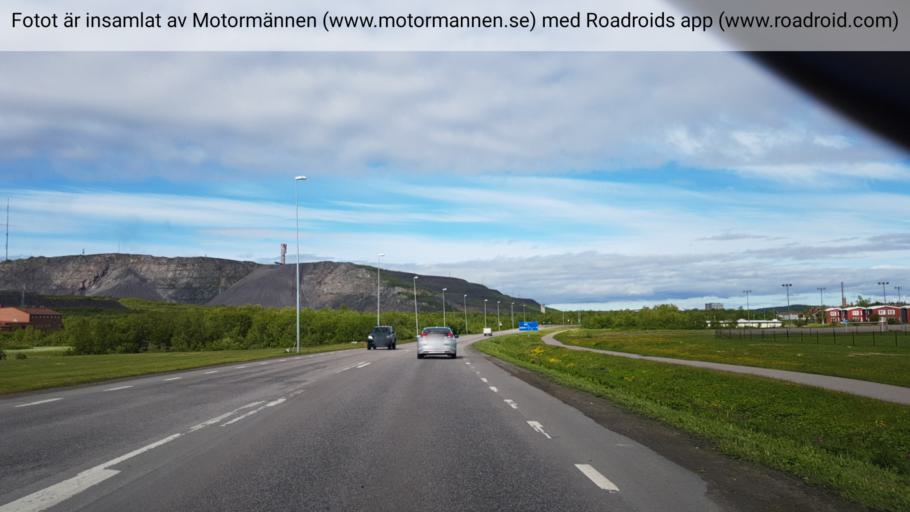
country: SE
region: Norrbotten
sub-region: Kiruna Kommun
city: Kiruna
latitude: 67.8426
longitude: 20.2397
